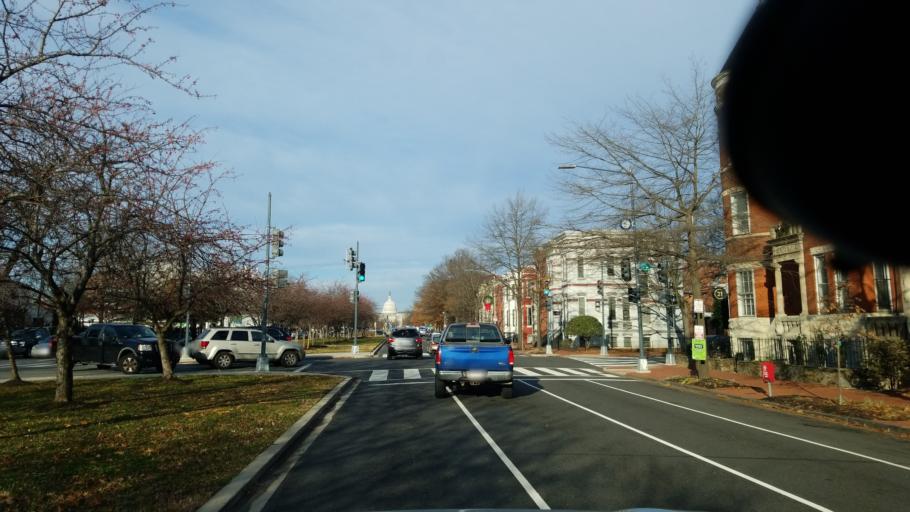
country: US
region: Washington, D.C.
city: Washington, D.C.
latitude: 38.8832
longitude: -76.9923
